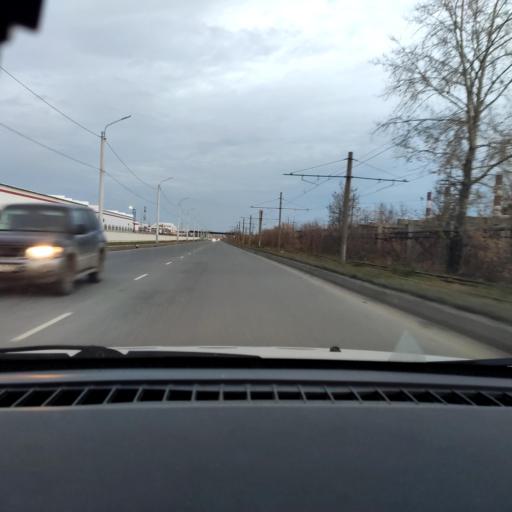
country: RU
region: Perm
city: Gamovo
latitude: 57.9170
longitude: 56.1506
